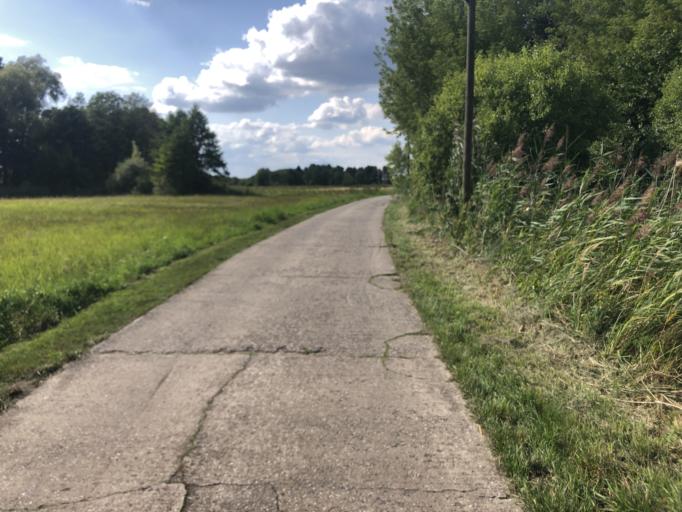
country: DE
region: Brandenburg
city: Mullrose
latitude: 52.2504
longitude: 14.4090
